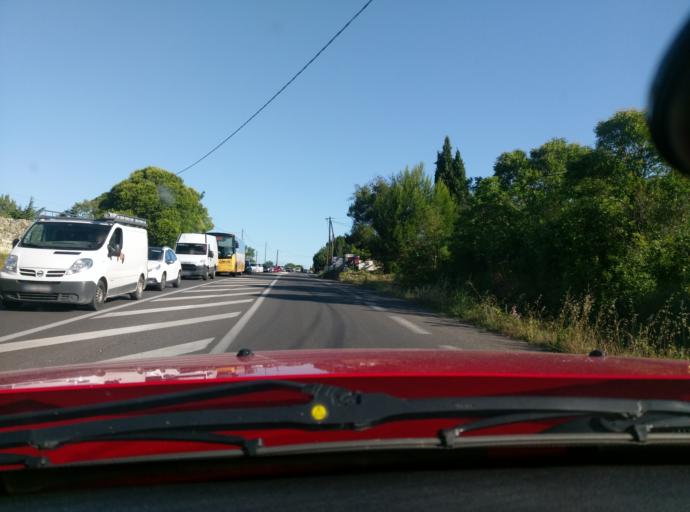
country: FR
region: Languedoc-Roussillon
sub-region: Departement du Gard
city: Uzes
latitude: 43.9947
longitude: 4.4186
